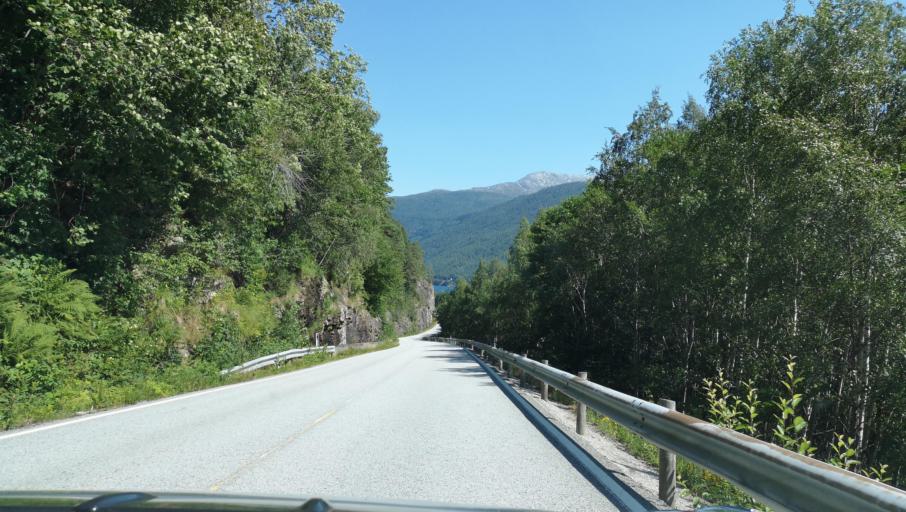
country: NO
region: Hordaland
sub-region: Ulvik
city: Ulvik
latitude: 60.4882
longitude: 6.8856
